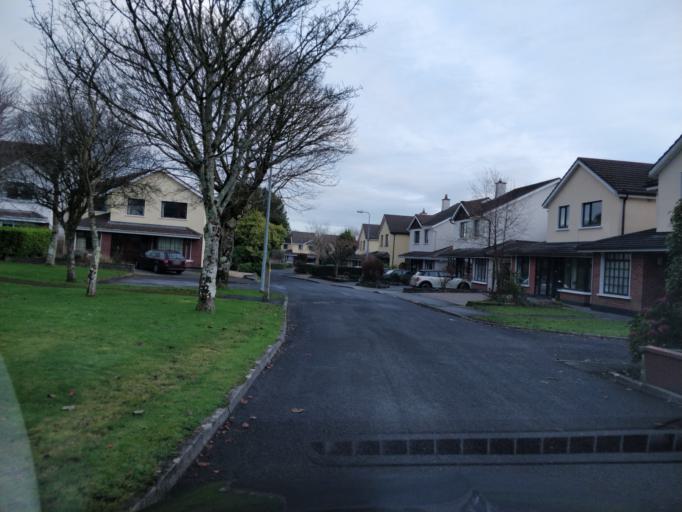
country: IE
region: Connaught
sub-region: County Galway
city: Bearna
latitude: 53.2642
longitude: -9.1087
